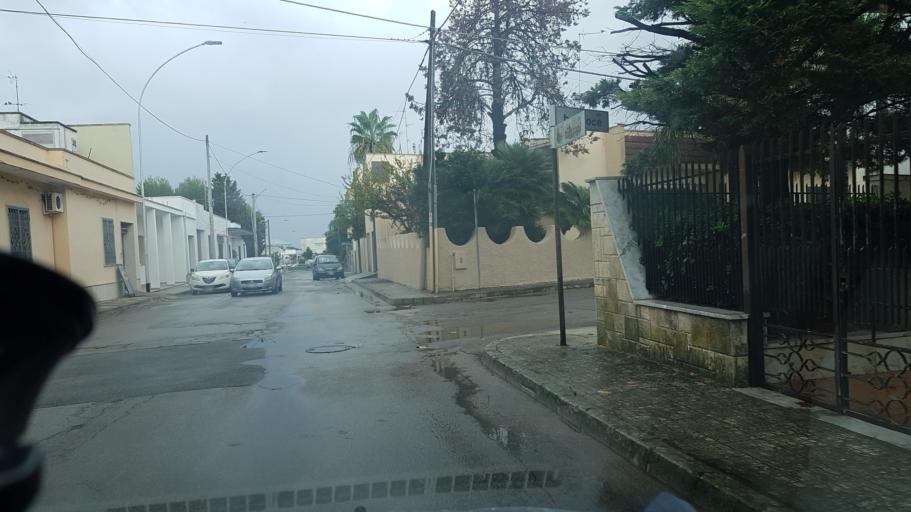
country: IT
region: Apulia
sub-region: Provincia di Lecce
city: Carmiano
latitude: 40.3436
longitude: 18.0500
